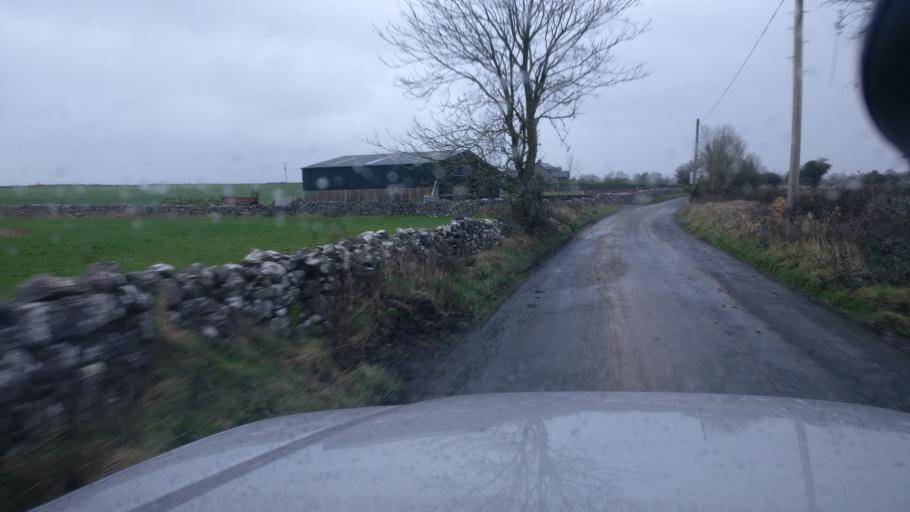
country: IE
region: Connaught
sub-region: County Galway
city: Loughrea
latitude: 53.2306
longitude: -8.6107
